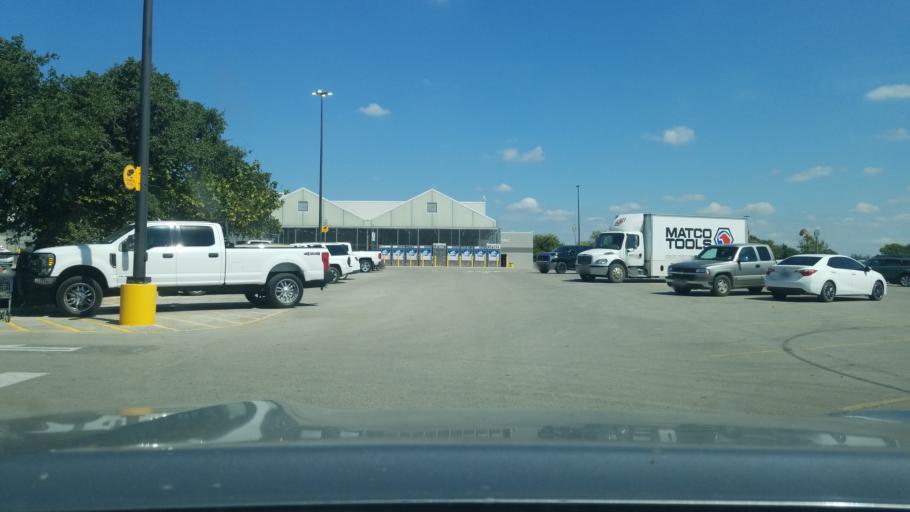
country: US
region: Texas
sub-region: Kendall County
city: Boerne
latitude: 29.7775
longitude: -98.7244
